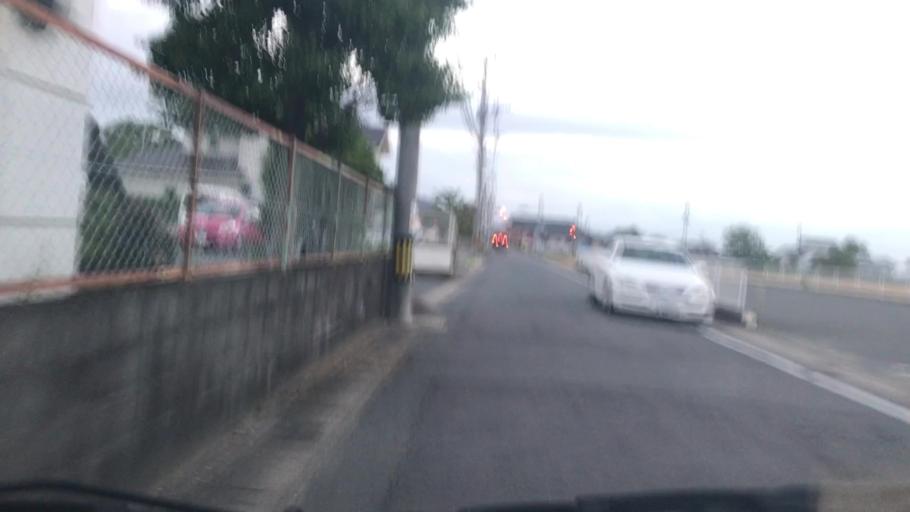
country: JP
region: Saga Prefecture
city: Saga-shi
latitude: 33.2294
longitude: 130.3020
